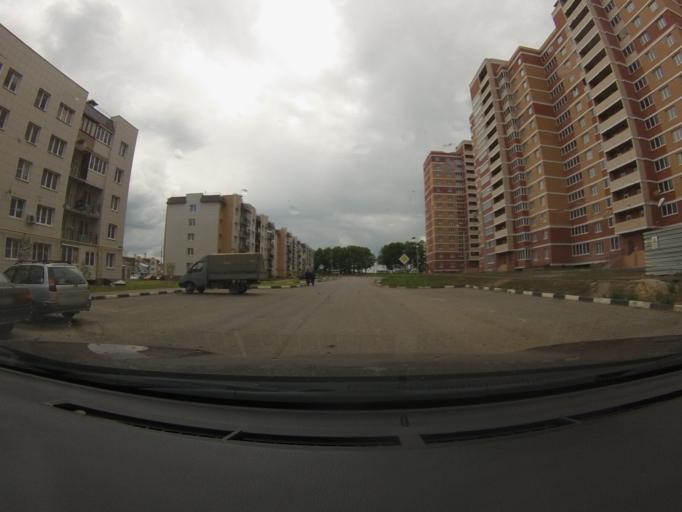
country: RU
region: Tula
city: Tula
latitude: 54.1743
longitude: 37.6542
